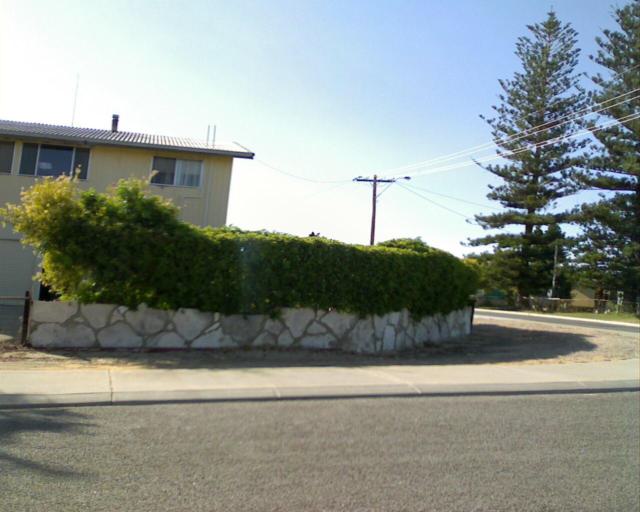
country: AU
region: Western Australia
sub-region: Dandaragan
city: Jurien Bay
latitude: -30.0701
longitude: 114.9701
